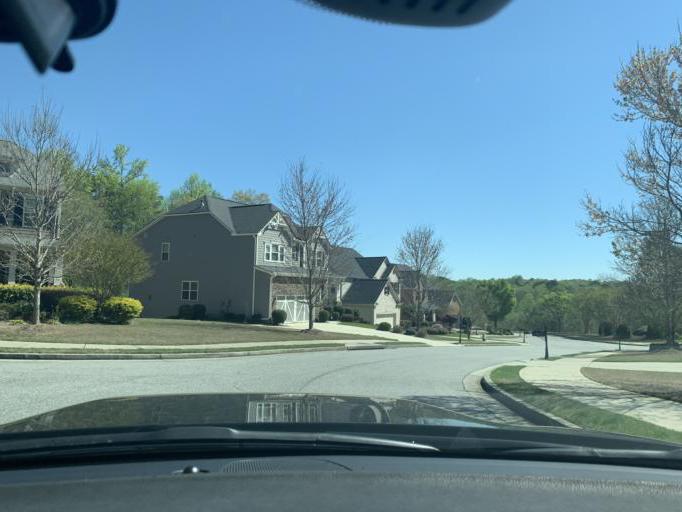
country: US
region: Georgia
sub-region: Fulton County
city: Milton
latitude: 34.1359
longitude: -84.2218
